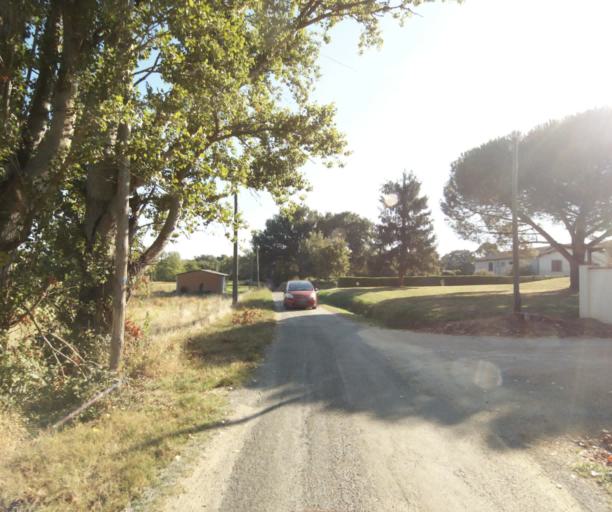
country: FR
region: Midi-Pyrenees
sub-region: Departement du Tarn-et-Garonne
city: Verdun-sur-Garonne
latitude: 43.8627
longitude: 1.2217
